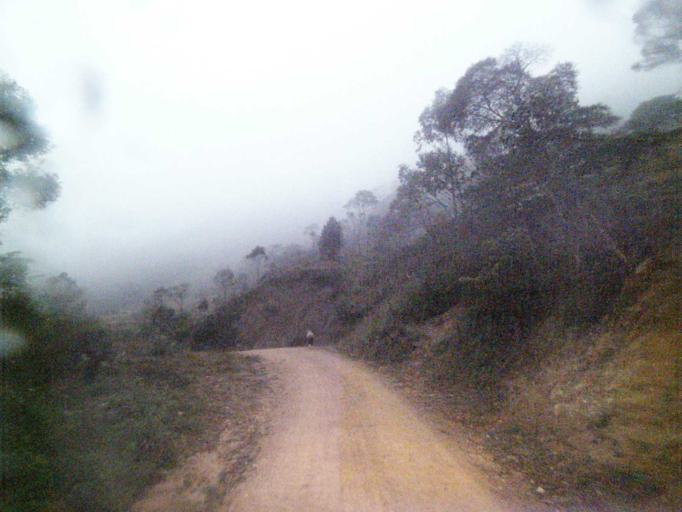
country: BR
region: Santa Catarina
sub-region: Anitapolis
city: Anitapolis
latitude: -27.7955
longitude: -49.1384
